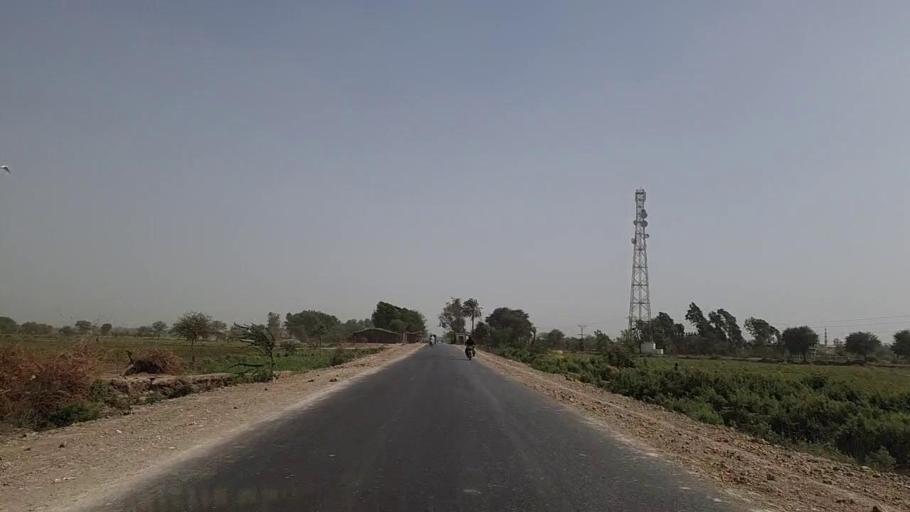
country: PK
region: Sindh
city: Tando Bago
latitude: 24.8169
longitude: 68.9071
